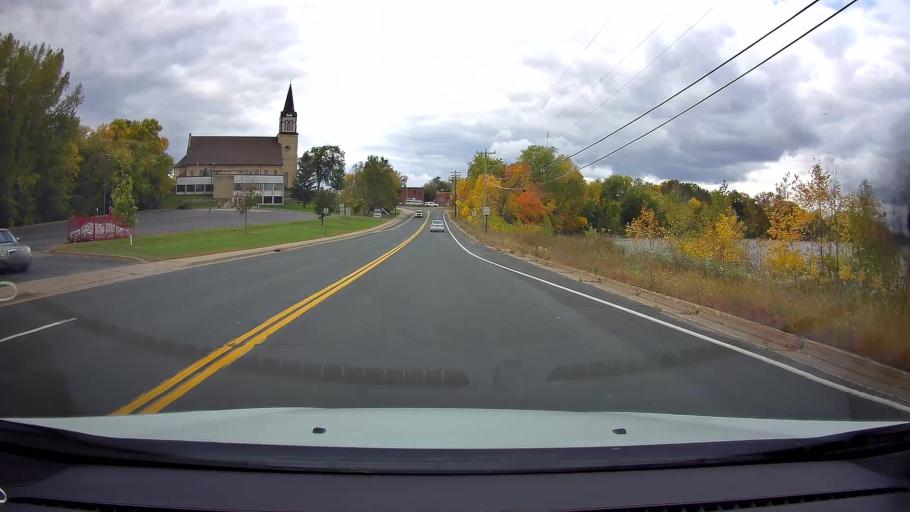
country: US
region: Minnesota
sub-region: Chisago County
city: Center City
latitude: 45.3974
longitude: -92.8161
